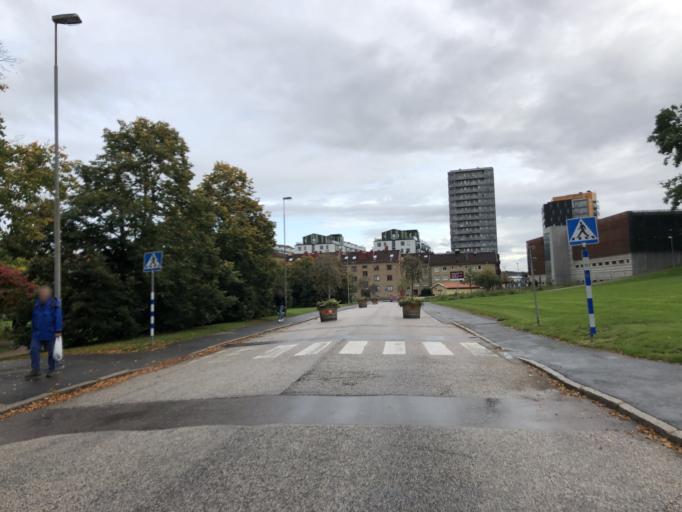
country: SE
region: Vaestra Goetaland
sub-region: Molndal
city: Moelndal
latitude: 57.6575
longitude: 12.0107
